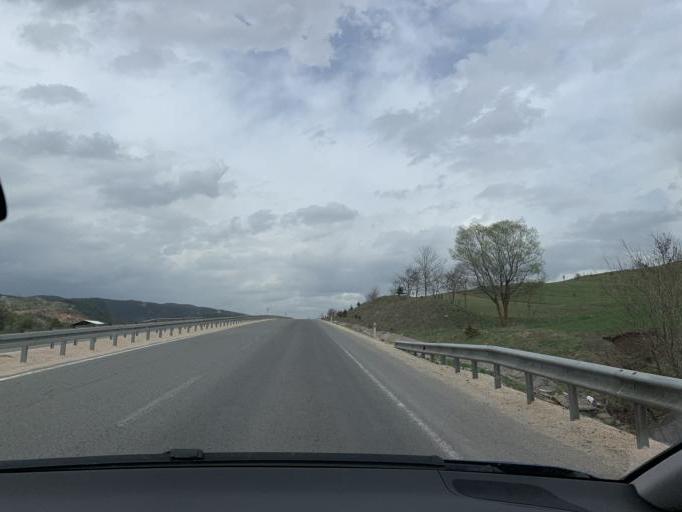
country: TR
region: Bolu
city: Gerede
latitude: 40.7917
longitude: 32.1380
